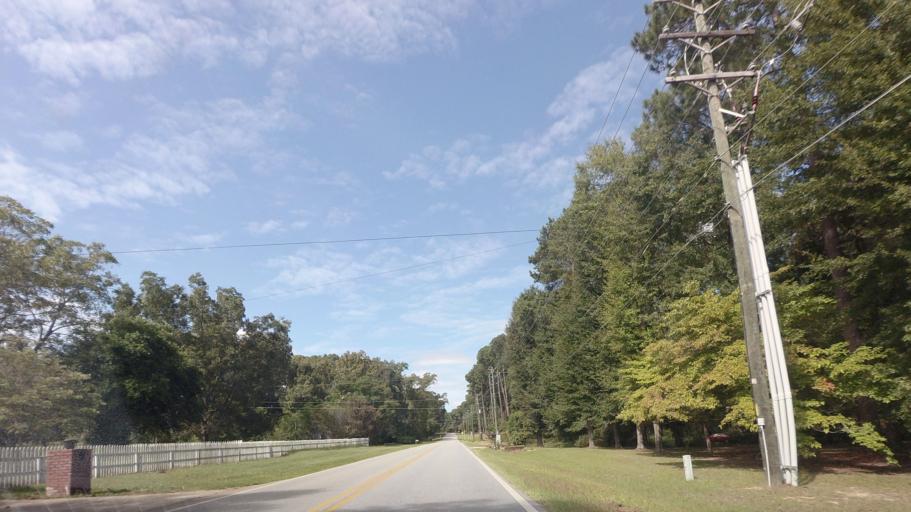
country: US
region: Georgia
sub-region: Houston County
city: Centerville
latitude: 32.6024
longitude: -83.7039
